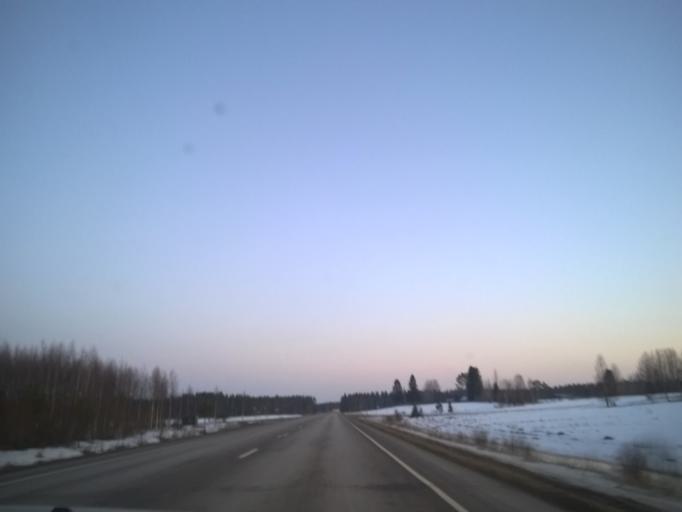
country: FI
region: Northern Ostrobothnia
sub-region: Nivala-Haapajaervi
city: Pyhaejaervi
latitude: 63.8016
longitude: 25.9152
